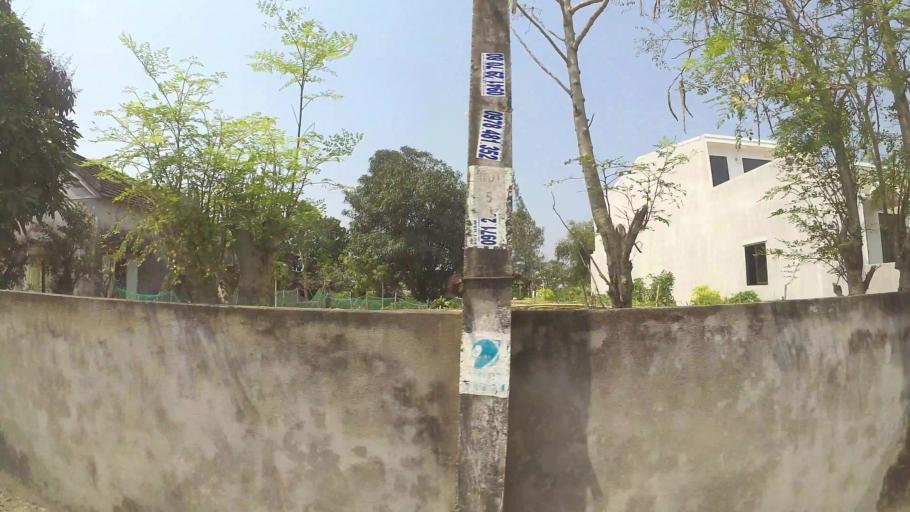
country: VN
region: Da Nang
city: Ngu Hanh Son
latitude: 15.9931
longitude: 108.2642
